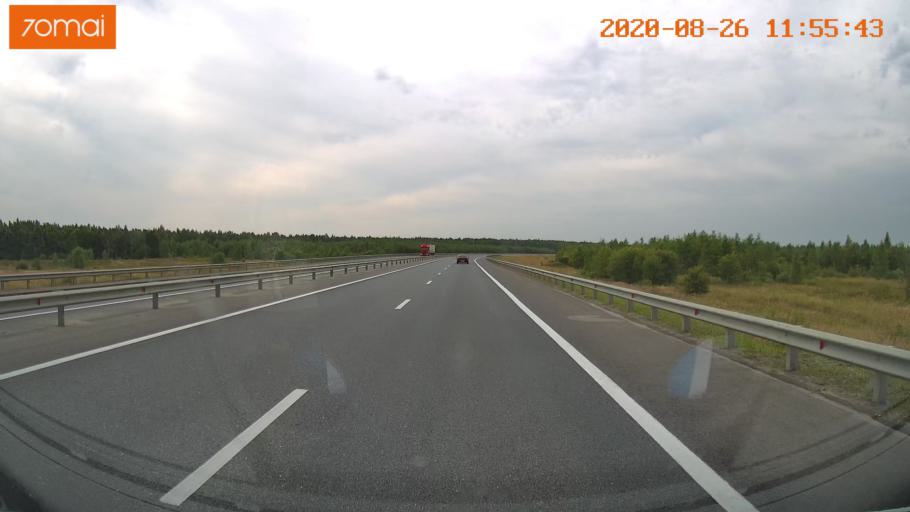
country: RU
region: Rjazan
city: Kiritsy
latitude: 54.2696
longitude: 40.3918
